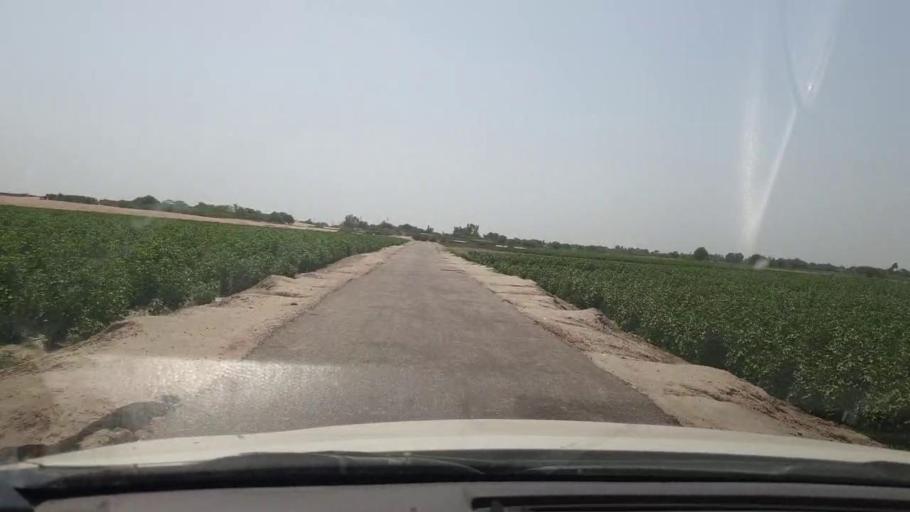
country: PK
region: Sindh
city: Rohri
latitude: 27.5225
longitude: 69.0619
